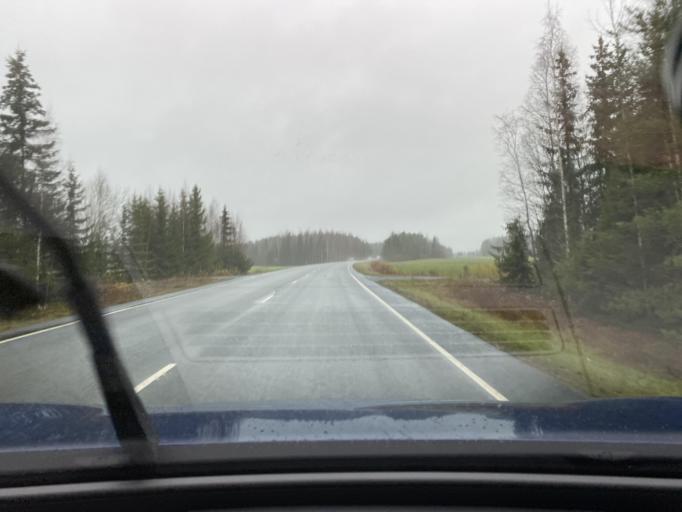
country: FI
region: Varsinais-Suomi
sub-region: Loimaa
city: Alastaro
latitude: 60.9202
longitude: 22.8960
